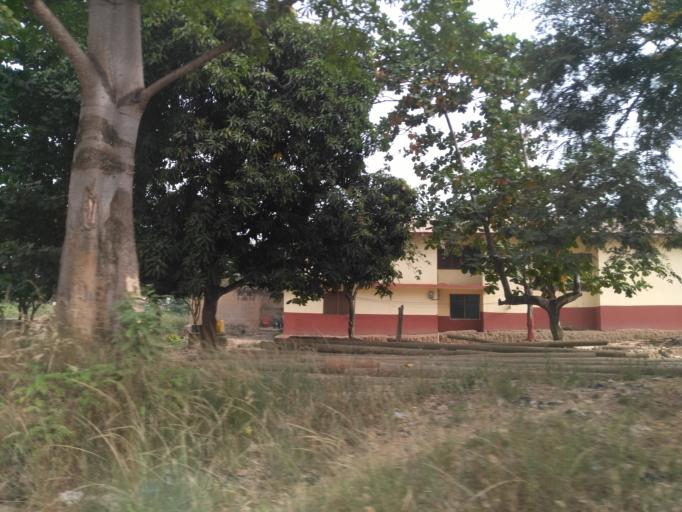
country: GH
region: Ashanti
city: Kumasi
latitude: 6.6402
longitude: -1.6262
